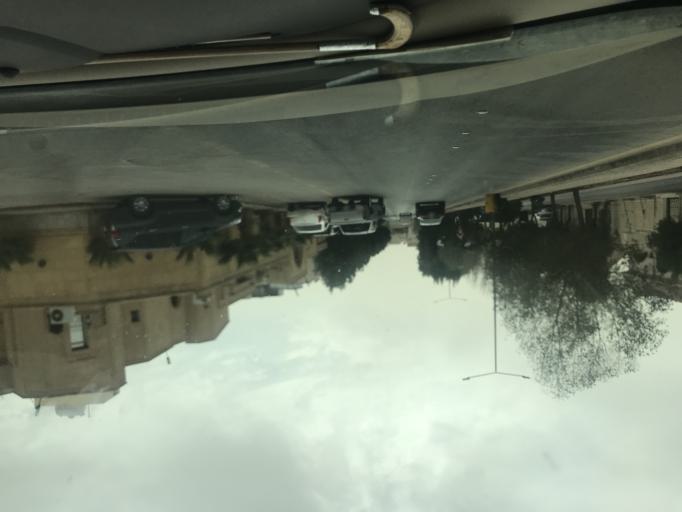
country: SA
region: Ar Riyad
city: Riyadh
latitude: 24.7397
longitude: 46.7560
